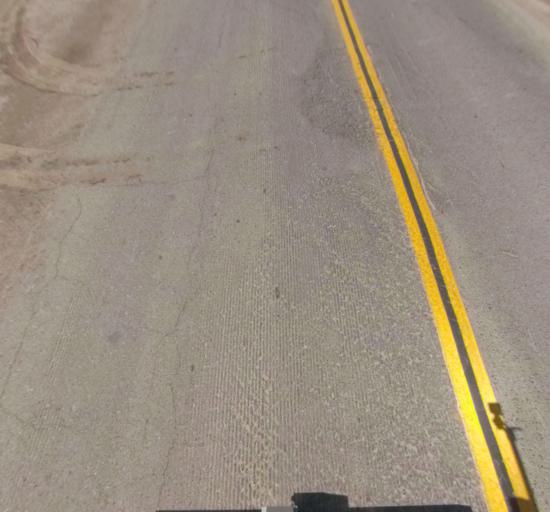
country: US
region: California
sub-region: Fresno County
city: Mendota
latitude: 36.8356
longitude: -120.2590
